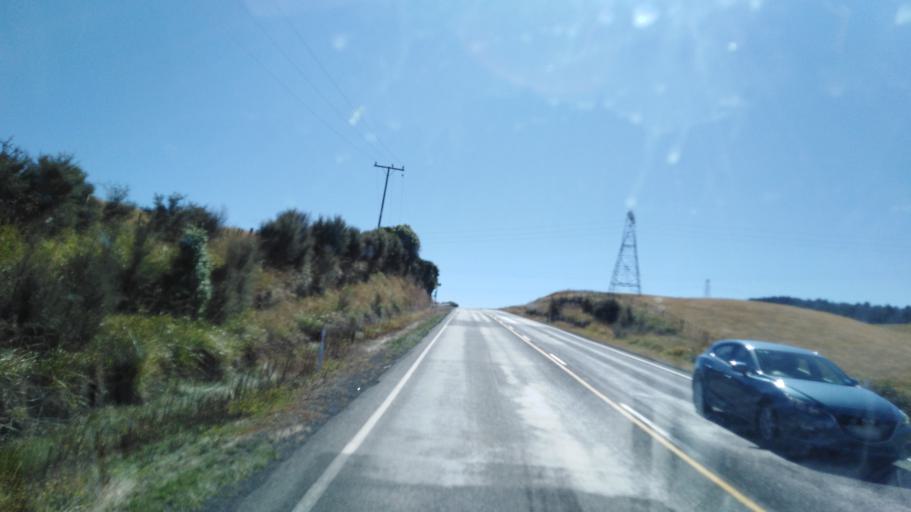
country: NZ
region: Manawatu-Wanganui
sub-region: Ruapehu District
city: Waiouru
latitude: -39.5317
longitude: 175.6824
